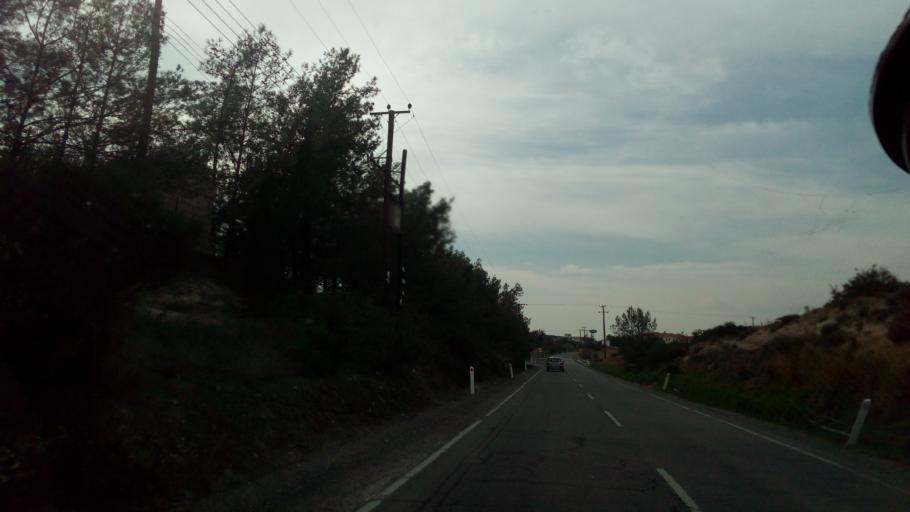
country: CY
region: Larnaka
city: Tersefanou
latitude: 34.8571
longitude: 33.4674
